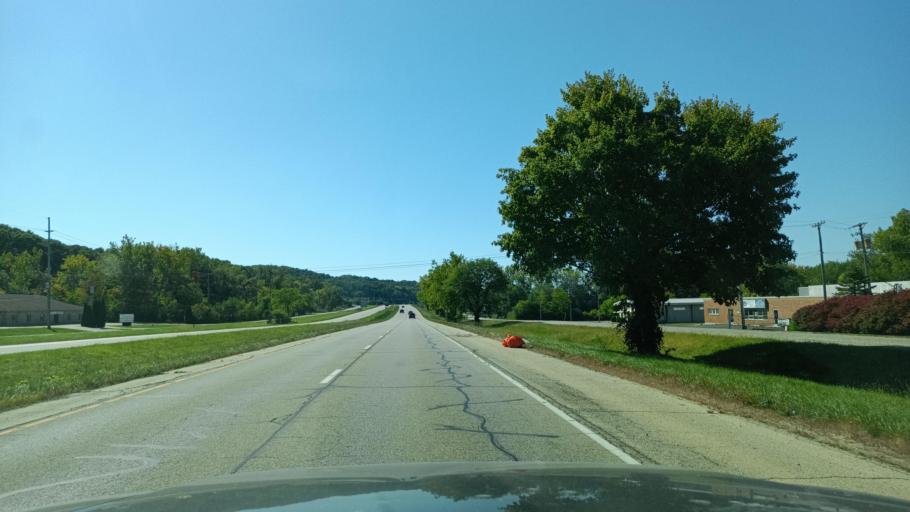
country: US
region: Illinois
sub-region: Peoria County
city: North Peoria
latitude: 40.7016
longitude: -89.5376
